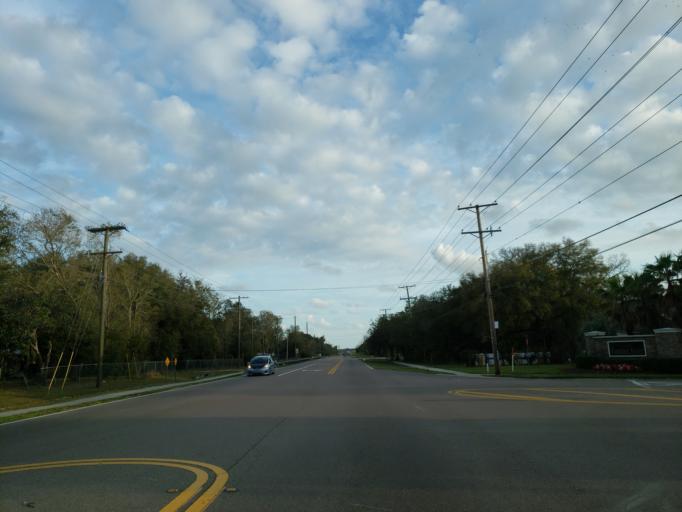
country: US
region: Florida
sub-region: Hillsborough County
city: Balm
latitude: 27.8085
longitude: -82.2908
